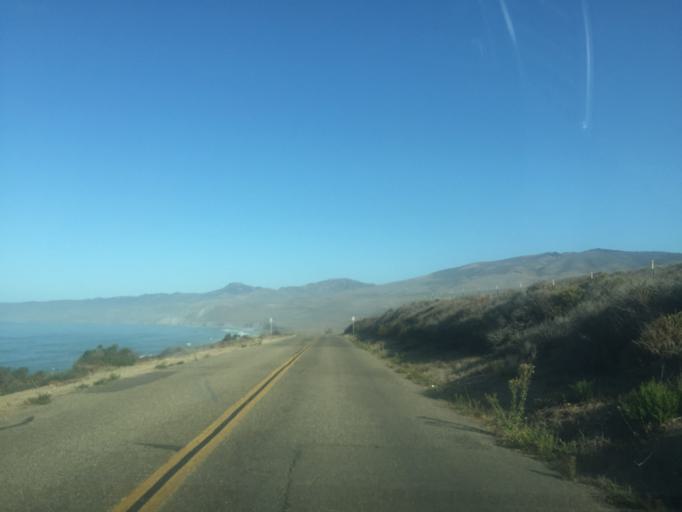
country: US
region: California
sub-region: Santa Barbara County
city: Lompoc
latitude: 34.5049
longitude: -120.4981
